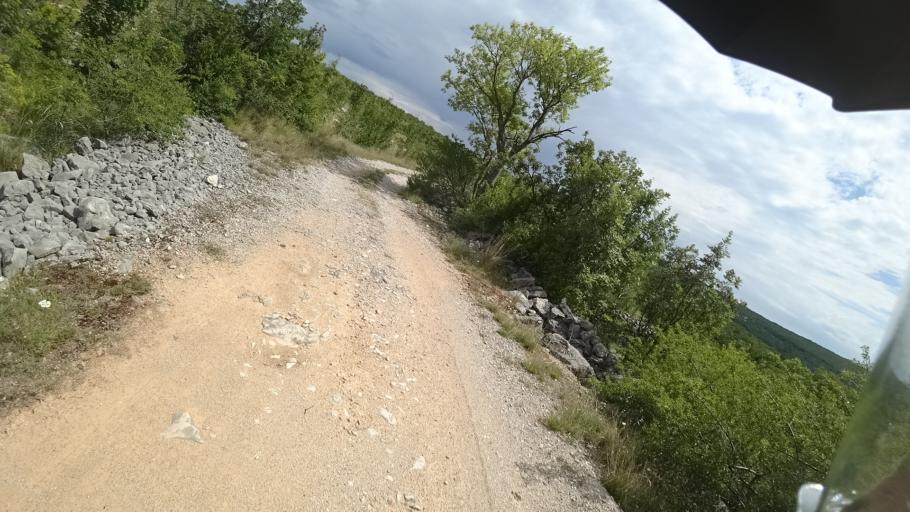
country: HR
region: Sibensko-Kniniska
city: Kistanje
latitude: 44.0932
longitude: 16.0421
